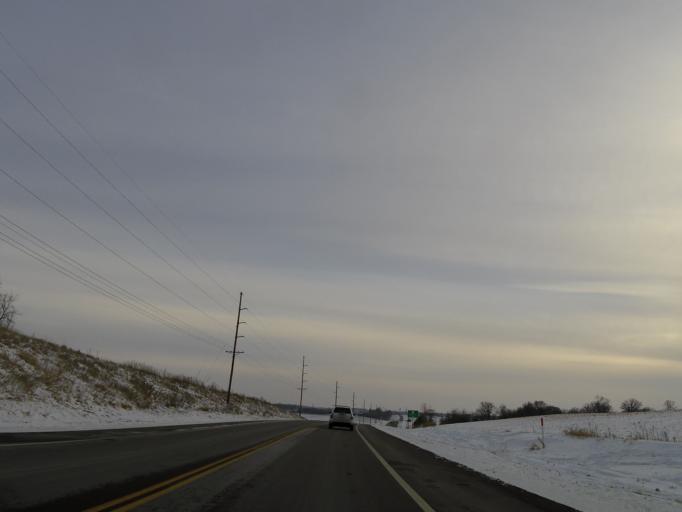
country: US
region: Minnesota
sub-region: Carver County
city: Victoria
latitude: 44.8284
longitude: -93.6525
